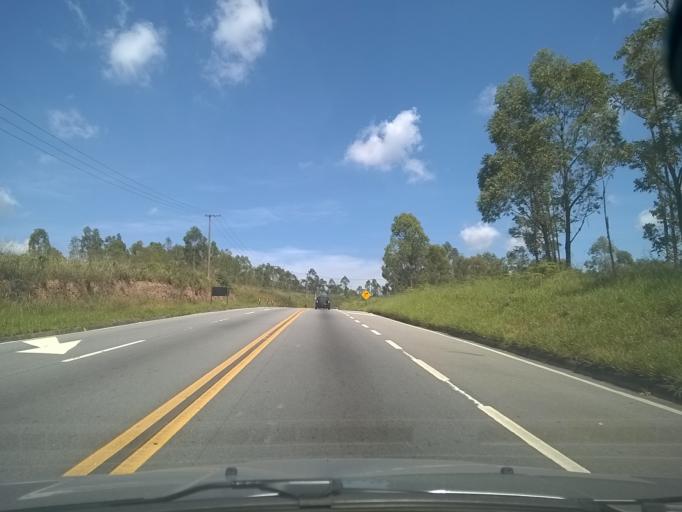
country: BR
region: Sao Paulo
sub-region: Francisco Morato
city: Francisco Morato
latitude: -23.2981
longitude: -46.7797
